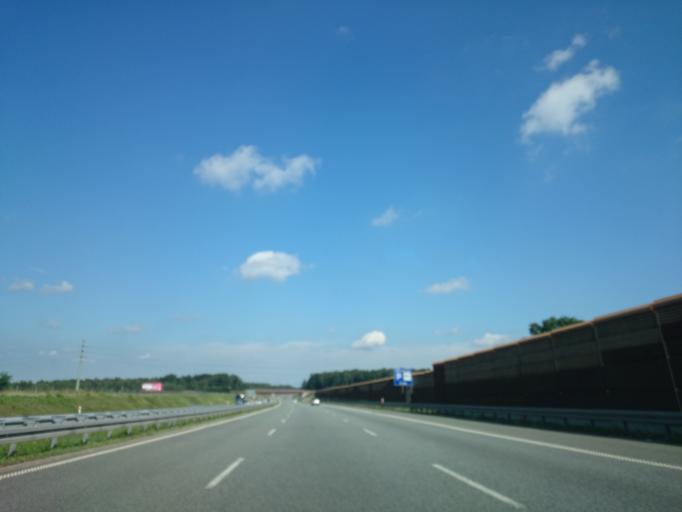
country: PL
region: Silesian Voivodeship
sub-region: Powiat mikolowski
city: Ornontowice
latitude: 50.1781
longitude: 18.7131
